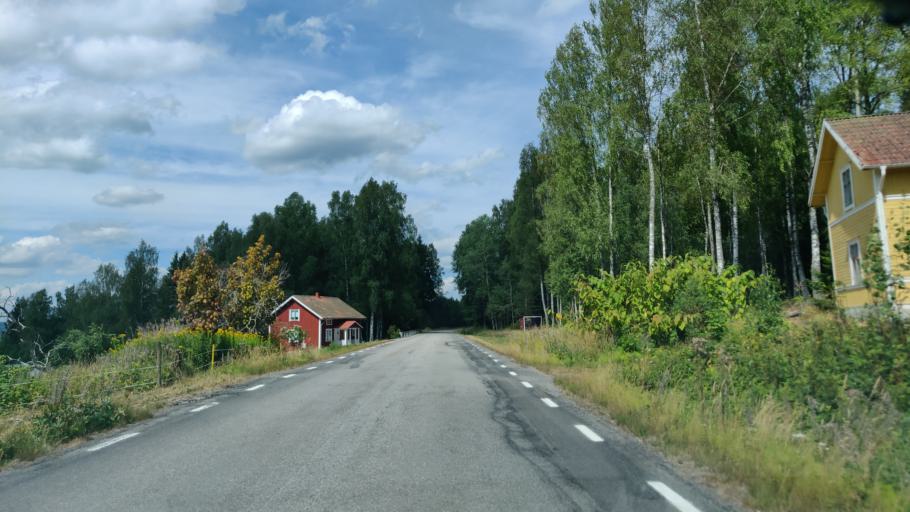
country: SE
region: Vaermland
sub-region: Hagfors Kommun
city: Ekshaerad
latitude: 60.0995
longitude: 13.5026
